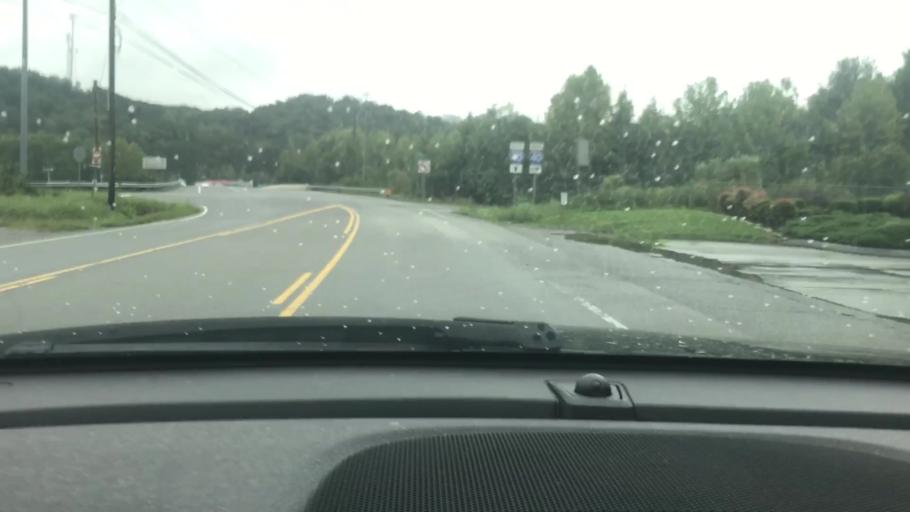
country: US
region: Tennessee
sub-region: Cheatham County
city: Kingston Springs
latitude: 36.0846
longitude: -87.0993
